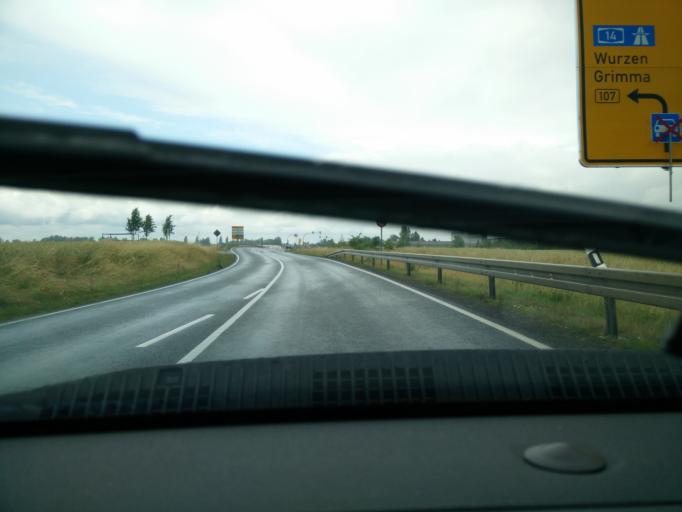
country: DE
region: Saxony
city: Grossbardau
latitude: 51.2170
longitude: 12.7085
